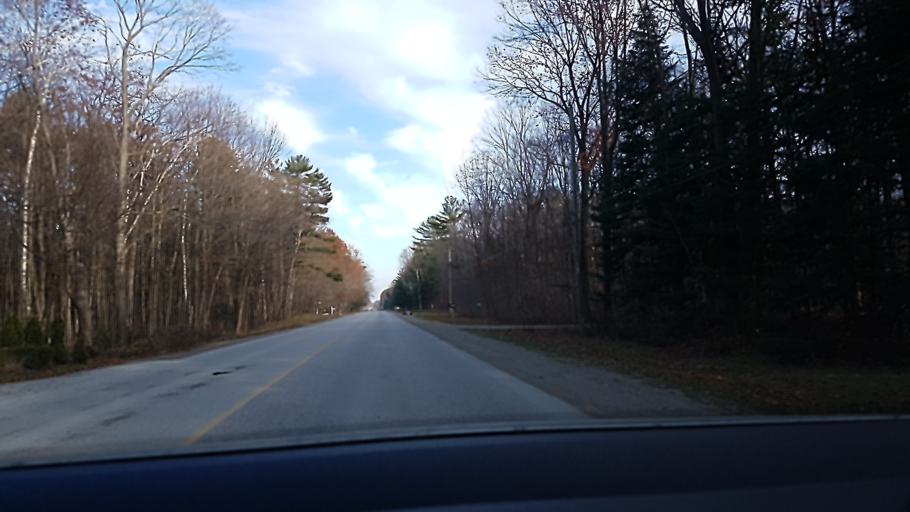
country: CA
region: Ontario
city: Barrie
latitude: 44.3925
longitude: -79.5481
